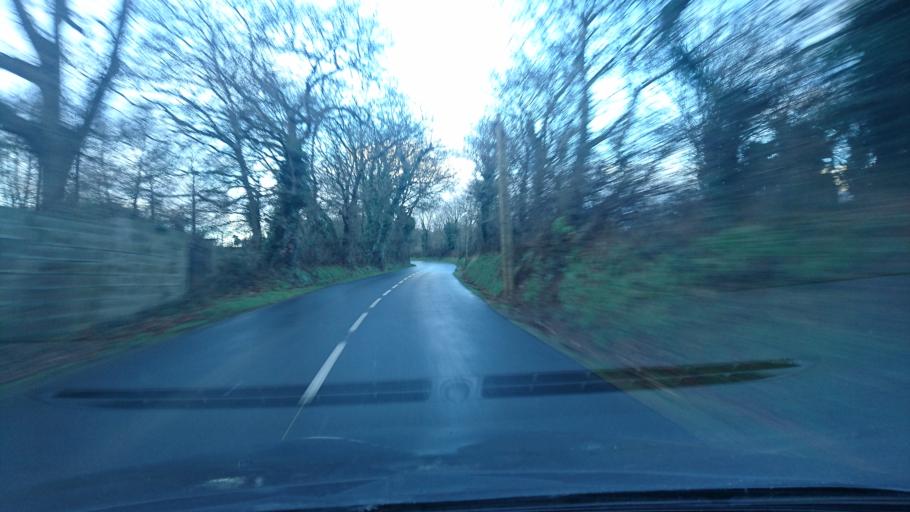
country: FR
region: Brittany
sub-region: Departement du Finistere
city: Guilers
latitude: 48.4060
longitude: -4.5516
